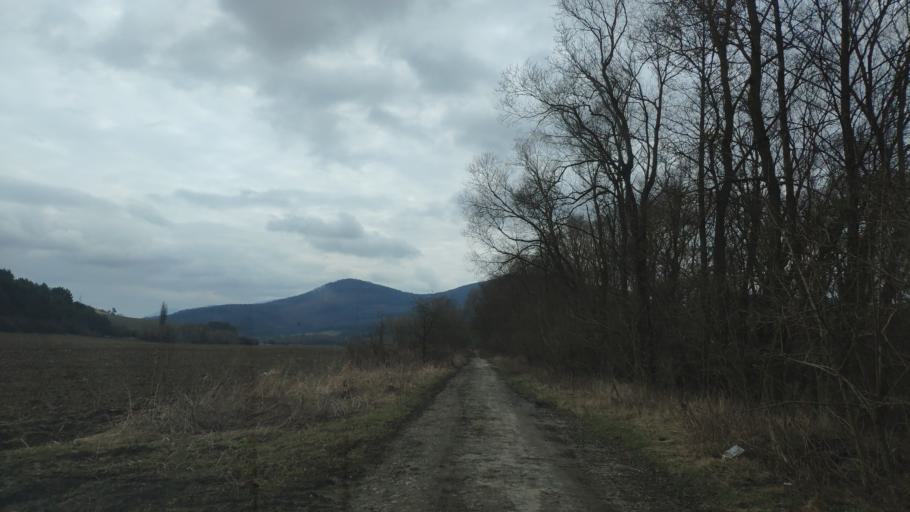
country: SK
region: Presovsky
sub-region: Okres Presov
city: Presov
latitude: 49.0861
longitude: 21.2834
